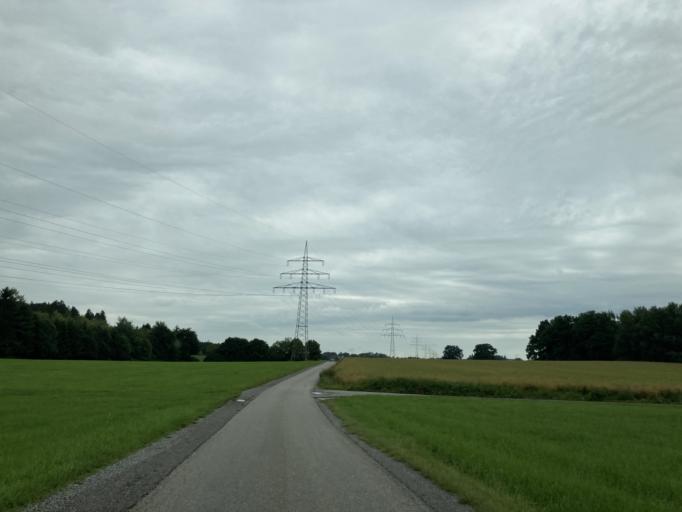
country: DE
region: Bavaria
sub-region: Upper Bavaria
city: Stephanskirchen
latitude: 47.8631
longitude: 12.1921
